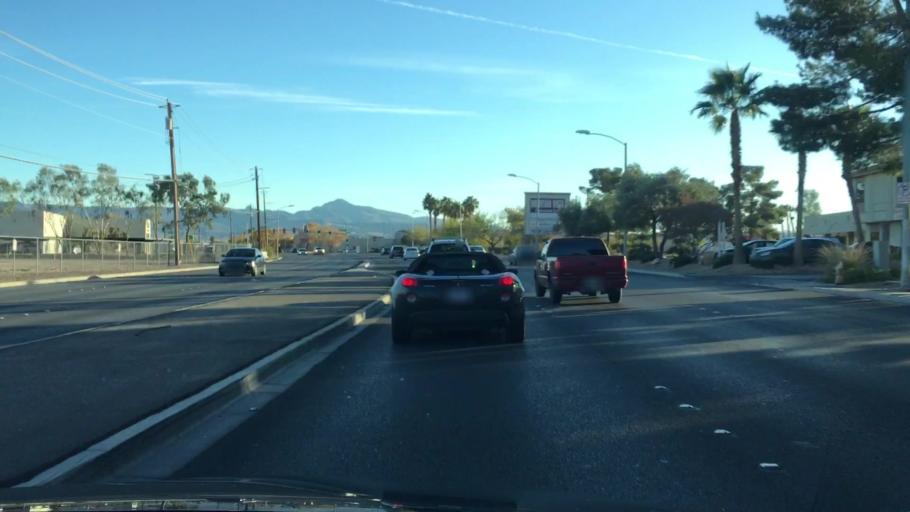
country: US
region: Nevada
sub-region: Clark County
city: Whitney
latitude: 36.0756
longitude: -115.0733
